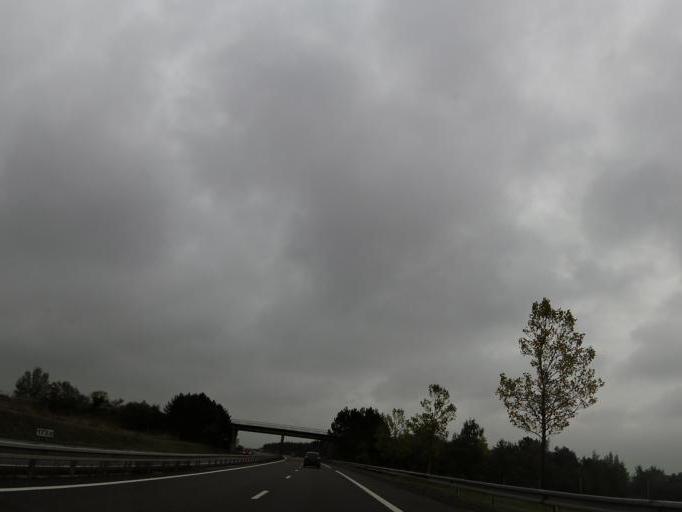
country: FR
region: Champagne-Ardenne
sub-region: Departement de la Marne
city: Chalons-en-Champagne
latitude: 49.0347
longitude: 4.3581
